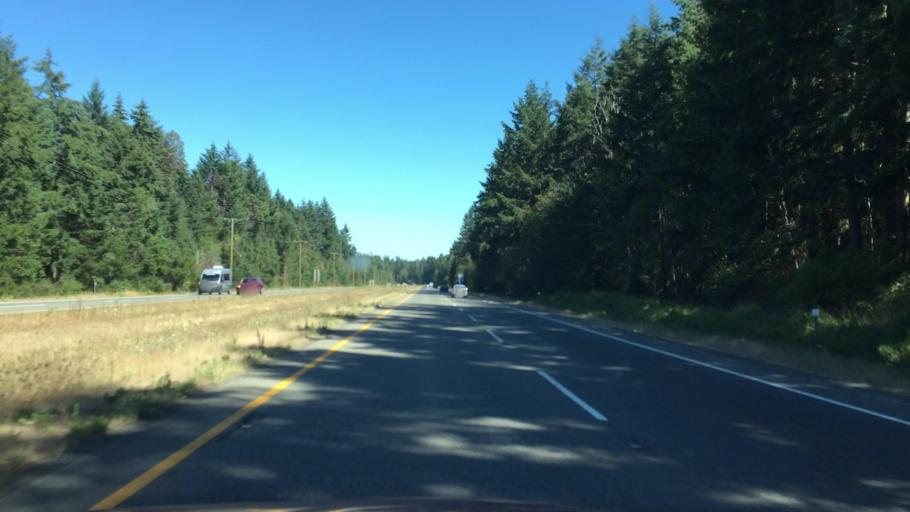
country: CA
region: British Columbia
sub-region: Regional District of Nanaimo
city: Parksville
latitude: 49.3008
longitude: -124.2951
